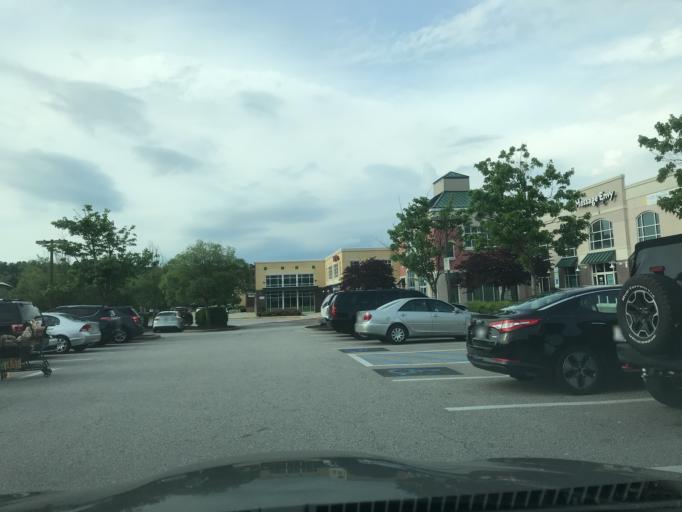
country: US
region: North Carolina
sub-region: Wake County
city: Wake Forest
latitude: 35.9053
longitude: -78.6003
